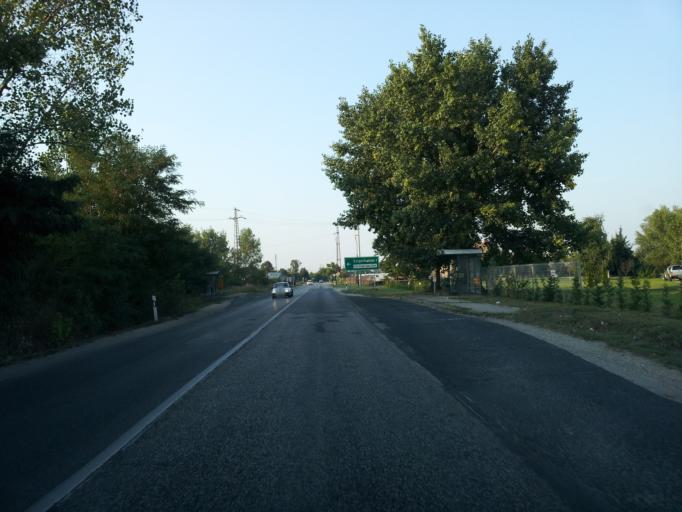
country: HU
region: Pest
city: Szigetszentmiklos
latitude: 47.3091
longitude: 19.0380
